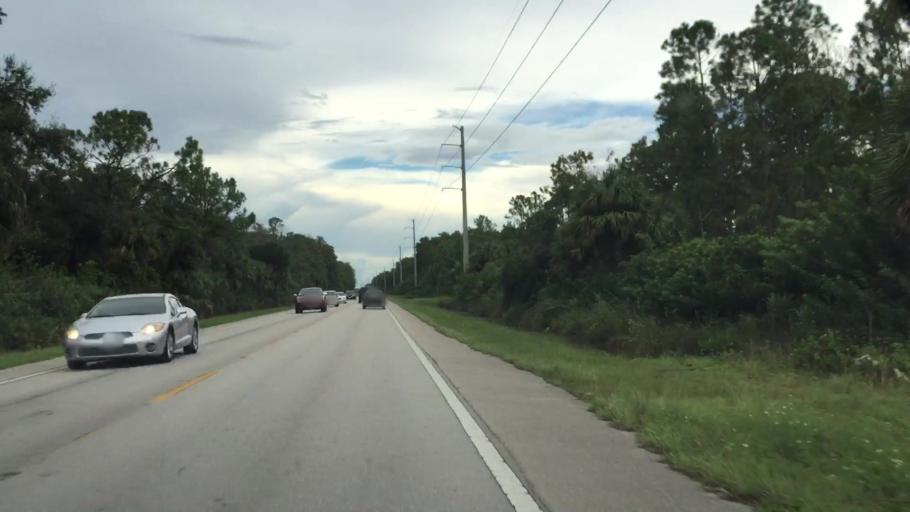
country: US
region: Florida
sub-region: Collier County
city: Orangetree
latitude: 26.3311
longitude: -81.5950
